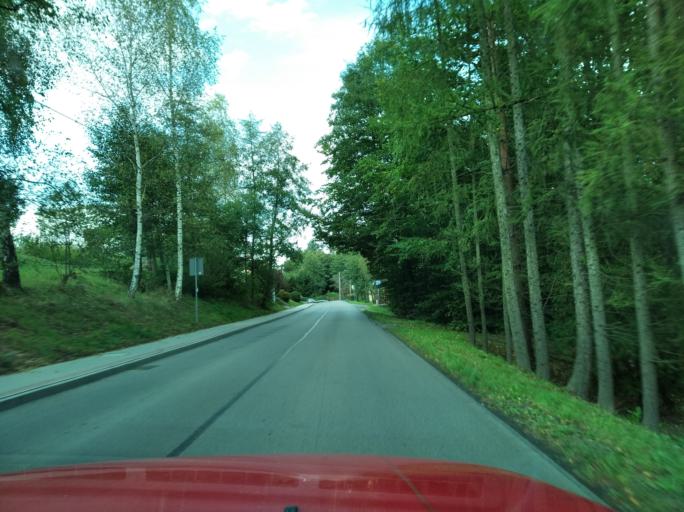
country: PL
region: Subcarpathian Voivodeship
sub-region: Powiat rzeszowski
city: Tyczyn
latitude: 49.9486
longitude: 22.0257
